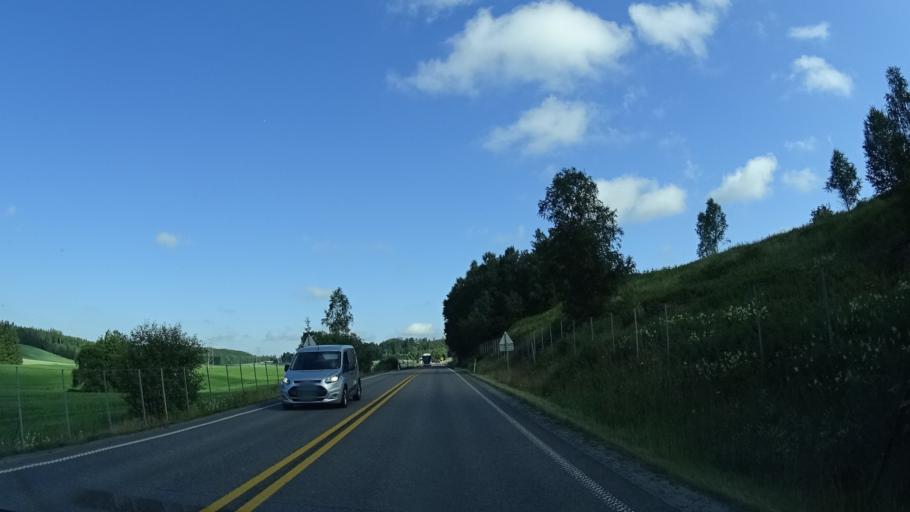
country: NO
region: Ostfold
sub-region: Hobol
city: Elvestad
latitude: 59.6506
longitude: 10.9219
